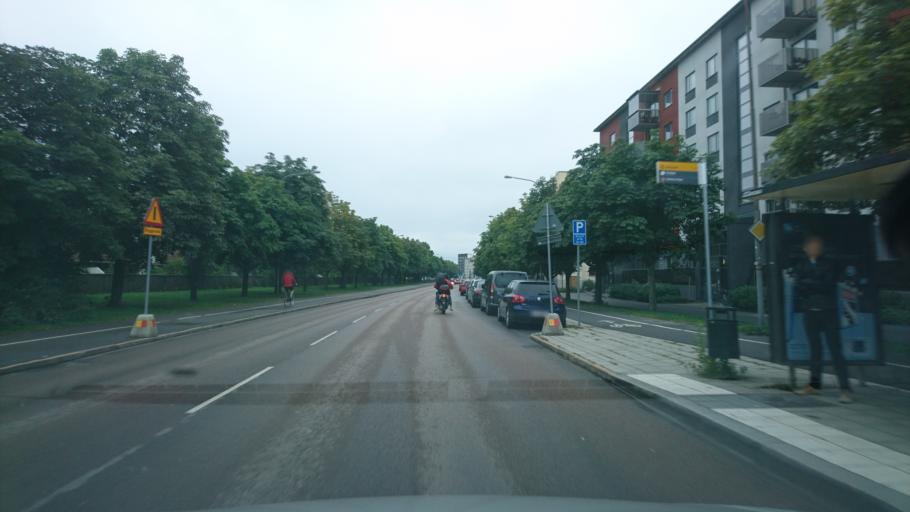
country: SE
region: Uppsala
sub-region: Uppsala Kommun
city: Uppsala
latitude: 59.8712
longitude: 17.6393
